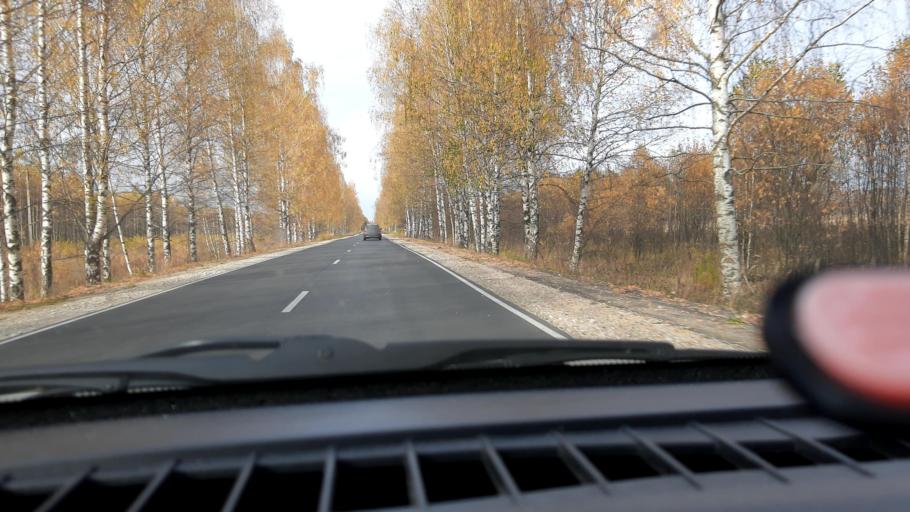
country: RU
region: Nizjnij Novgorod
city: Neklyudovo
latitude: 56.4912
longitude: 43.8602
